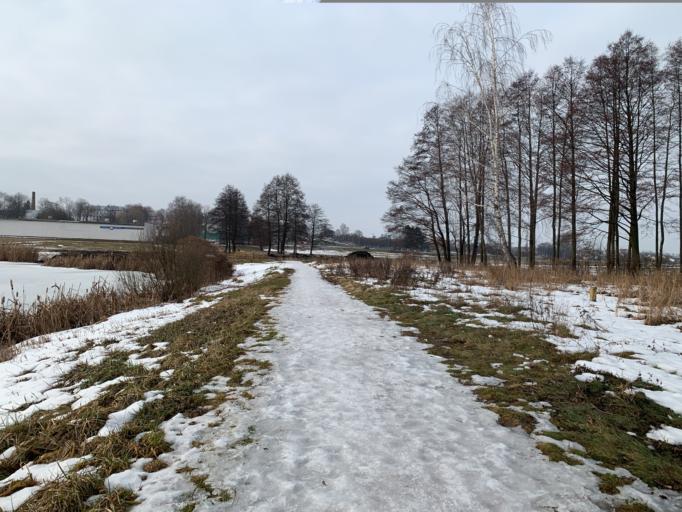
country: BY
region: Minsk
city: Nyasvizh
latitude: 53.2231
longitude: 26.6875
